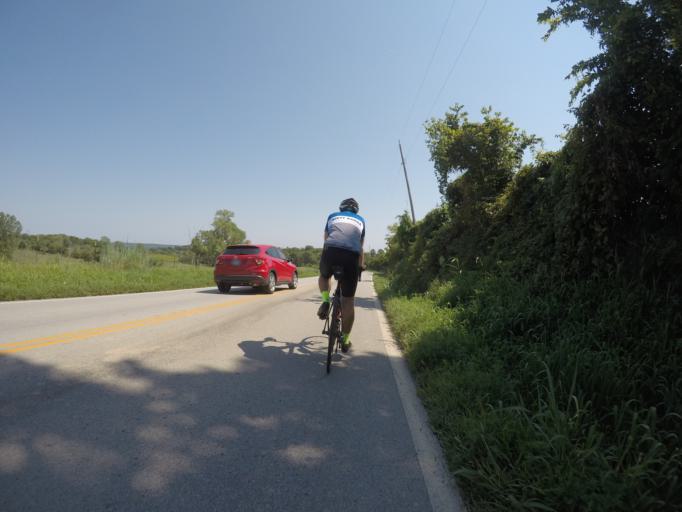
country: US
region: Kansas
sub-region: Leavenworth County
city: Lansing
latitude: 39.2398
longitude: -94.8680
